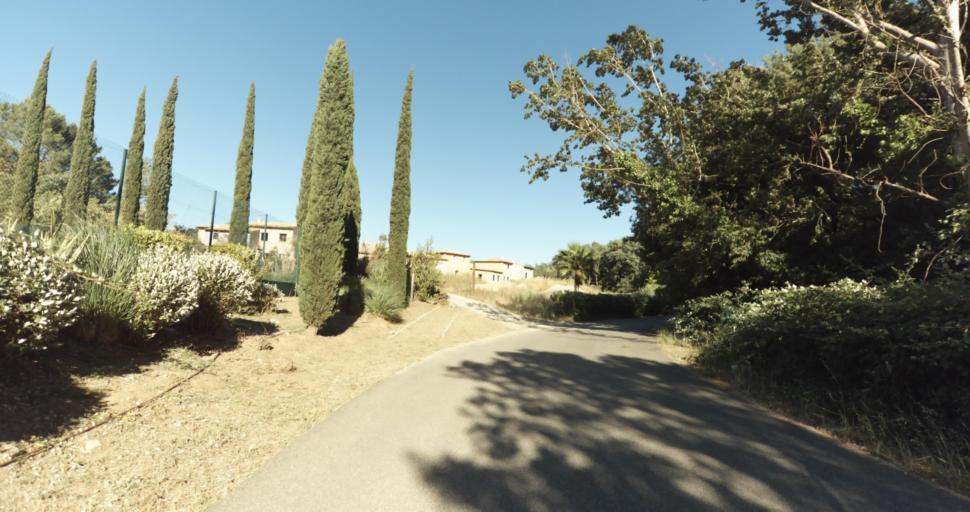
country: FR
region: Provence-Alpes-Cote d'Azur
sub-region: Departement du Var
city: Gassin
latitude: 43.2523
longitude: 6.6002
